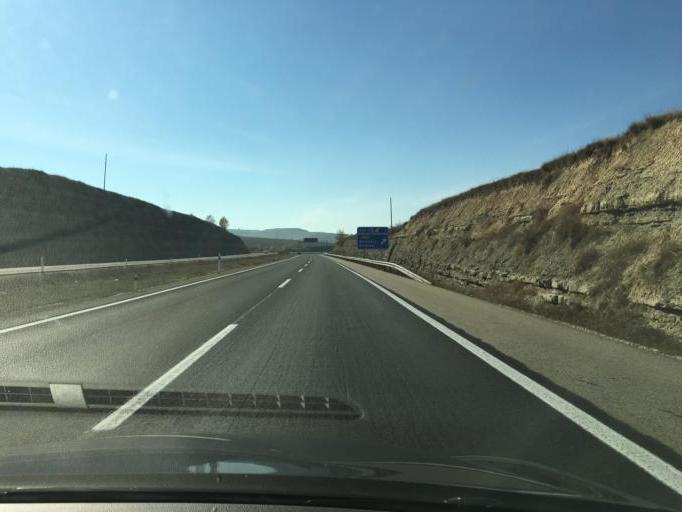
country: ES
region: Castille and Leon
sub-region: Provincia de Burgos
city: Briviesca
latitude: 42.5367
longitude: -3.3087
